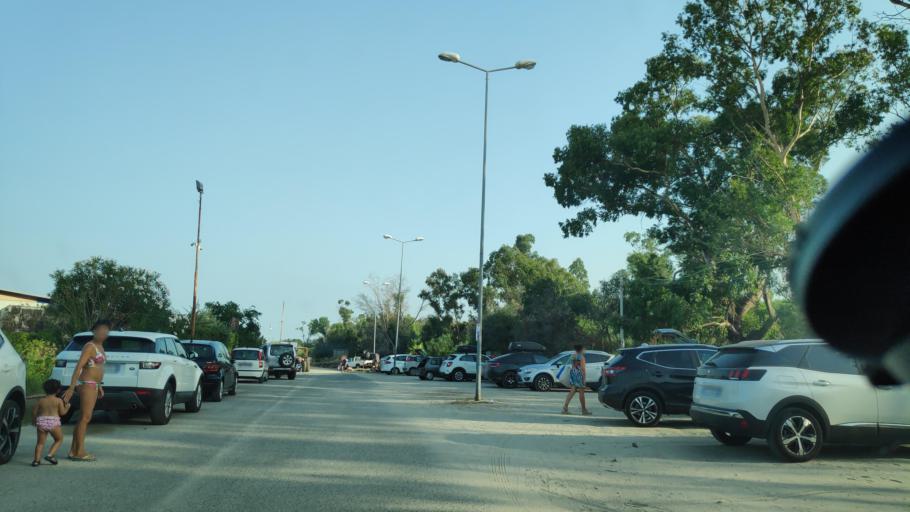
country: IT
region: Calabria
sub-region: Provincia di Catanzaro
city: Isca Marina
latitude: 38.6127
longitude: 16.5621
